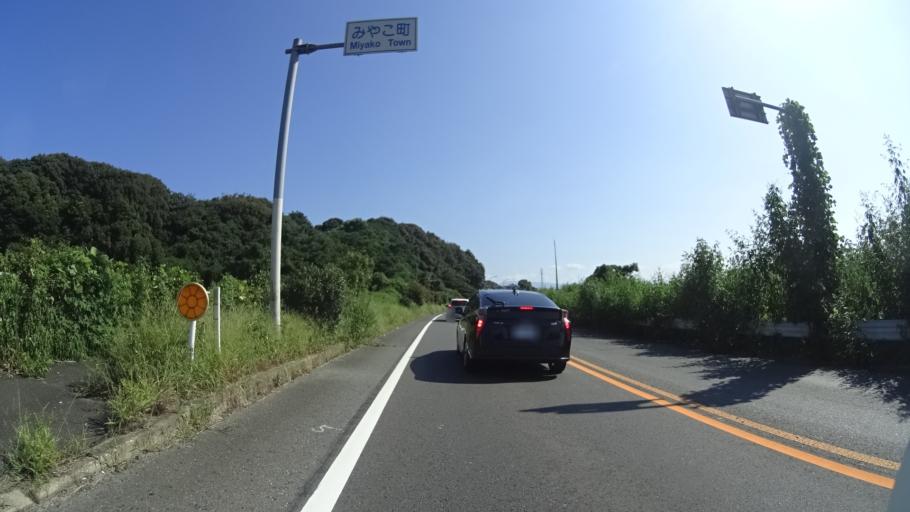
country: JP
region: Fukuoka
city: Yukuhashi
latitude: 33.6917
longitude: 130.9976
